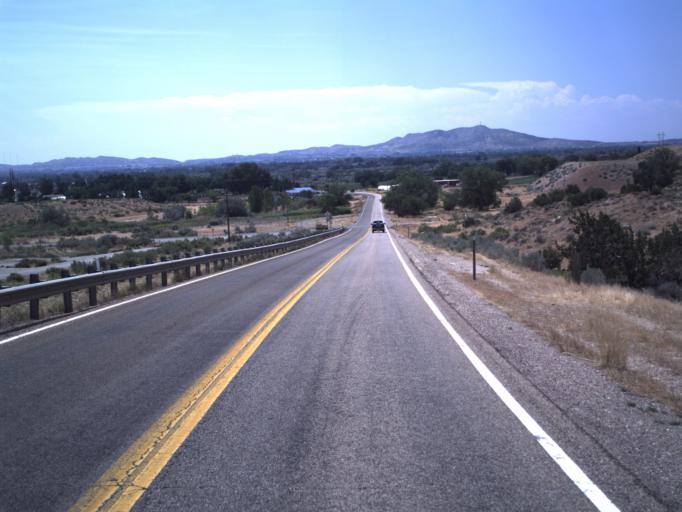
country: US
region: Utah
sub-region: Uintah County
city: Vernal
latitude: 40.5097
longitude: -109.5243
